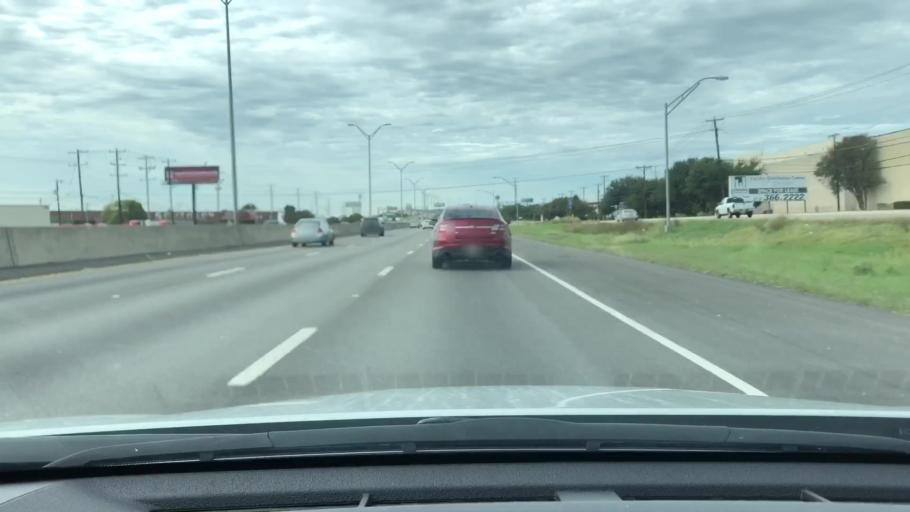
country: US
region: Texas
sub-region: Bexar County
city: Terrell Hills
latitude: 29.4455
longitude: -98.4321
